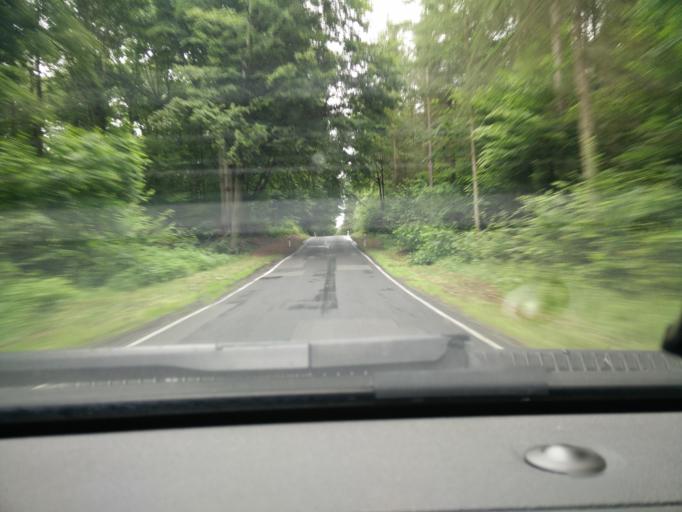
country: DE
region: Saxony
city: Grossbardau
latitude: 51.1674
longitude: 12.7010
